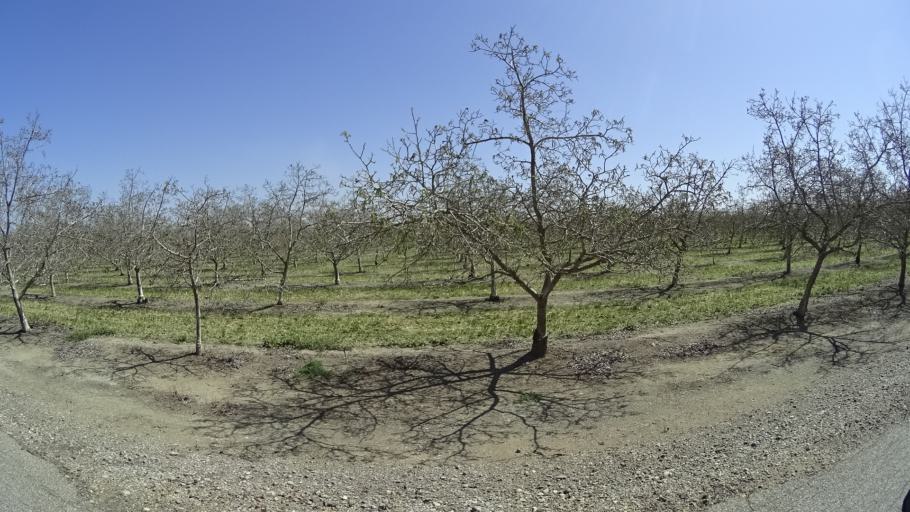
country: US
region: California
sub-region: Butte County
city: Durham
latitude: 39.4633
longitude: -121.9396
